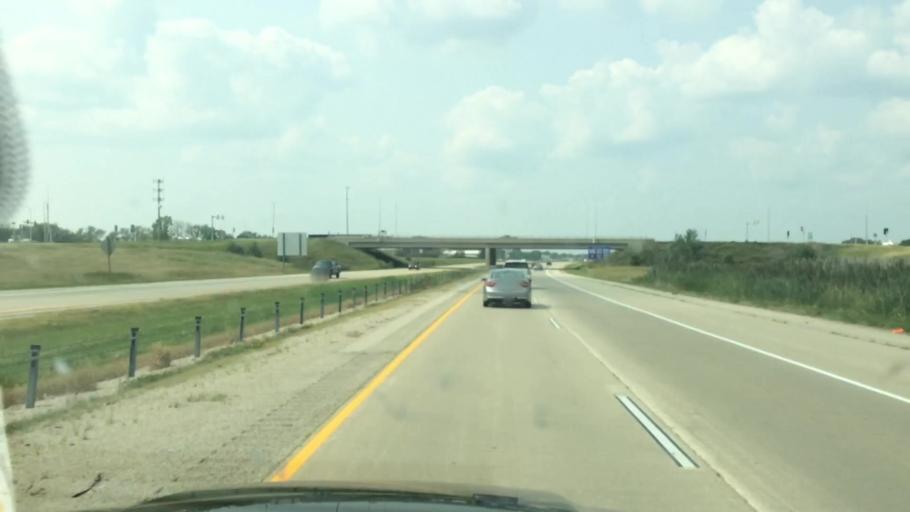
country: US
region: Wisconsin
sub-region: Fond du Lac County
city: Fond du Lac
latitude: 43.7571
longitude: -88.4730
